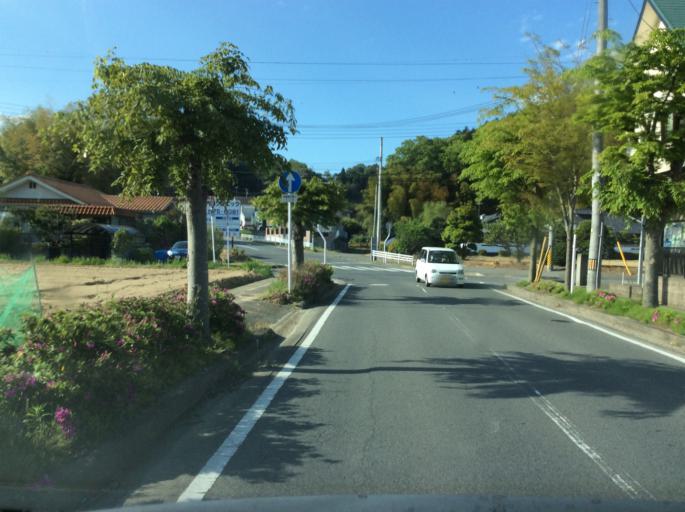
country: JP
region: Fukushima
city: Iwaki
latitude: 36.9603
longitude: 140.8498
